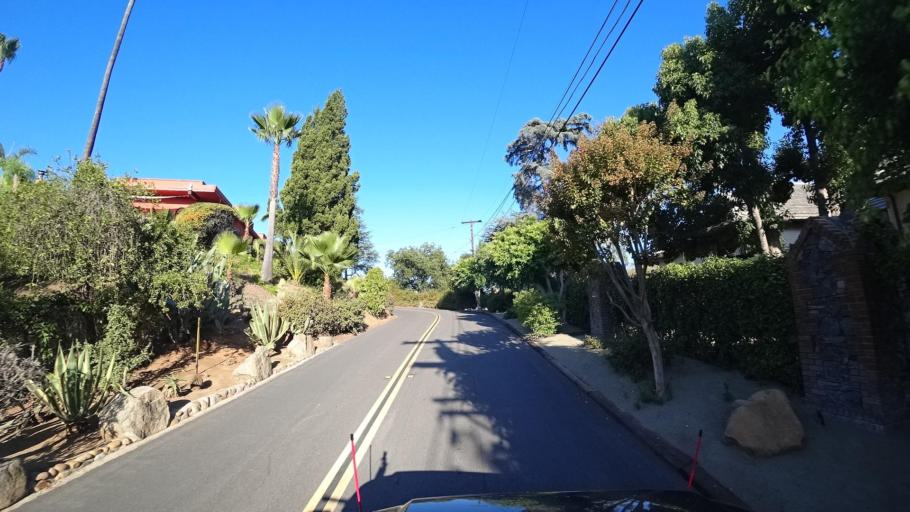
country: US
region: California
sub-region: San Diego County
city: Casa de Oro-Mount Helix
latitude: 32.7707
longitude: -116.9665
